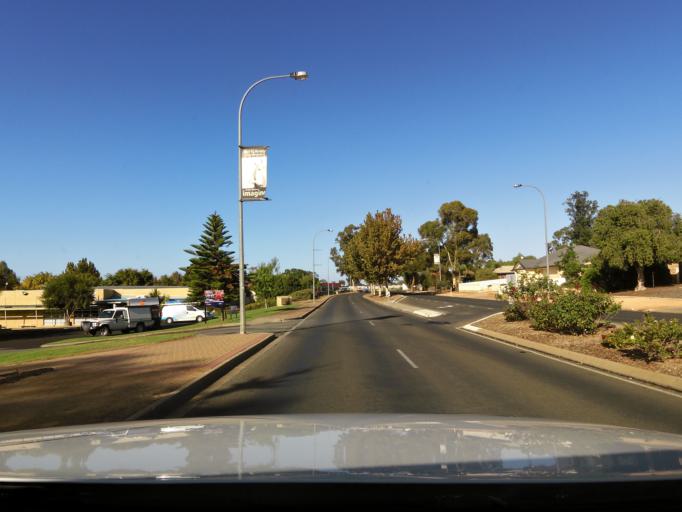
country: AU
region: South Australia
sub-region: Berri and Barmera
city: Berri
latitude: -34.2769
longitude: 140.6102
